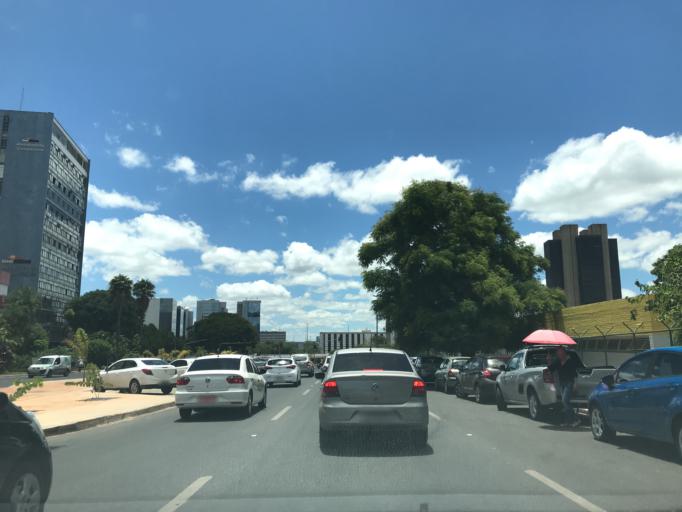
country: BR
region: Federal District
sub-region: Brasilia
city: Brasilia
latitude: -15.7995
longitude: -47.8884
